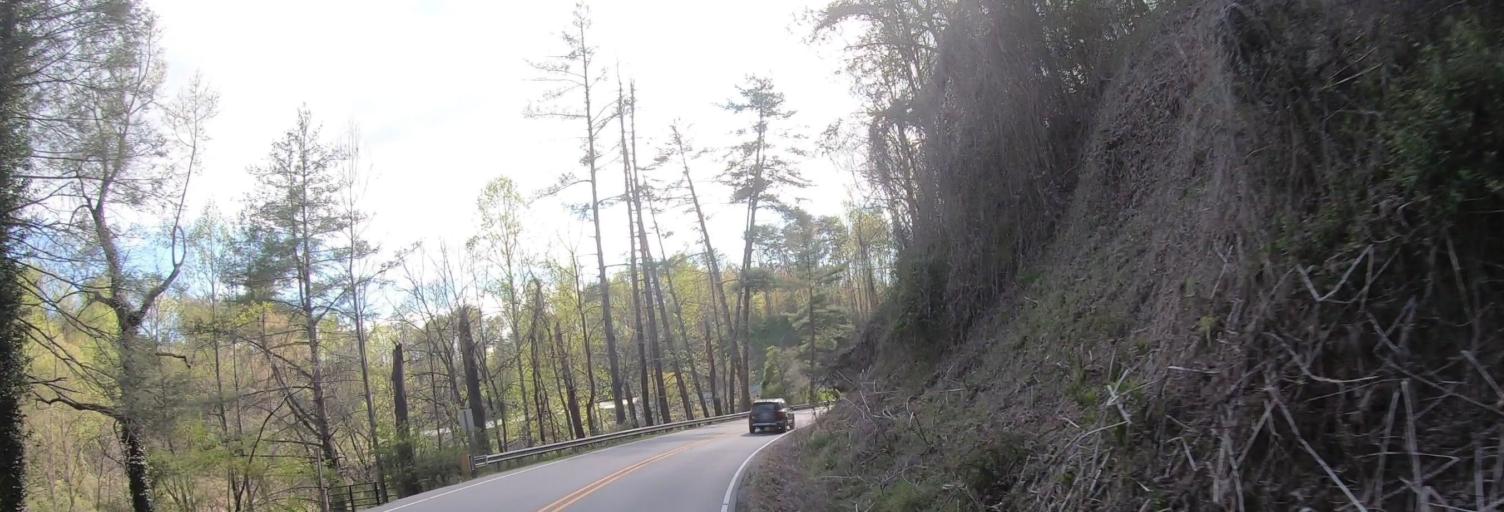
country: US
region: North Carolina
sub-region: Swain County
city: Cherokee
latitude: 35.4563
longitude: -83.3701
